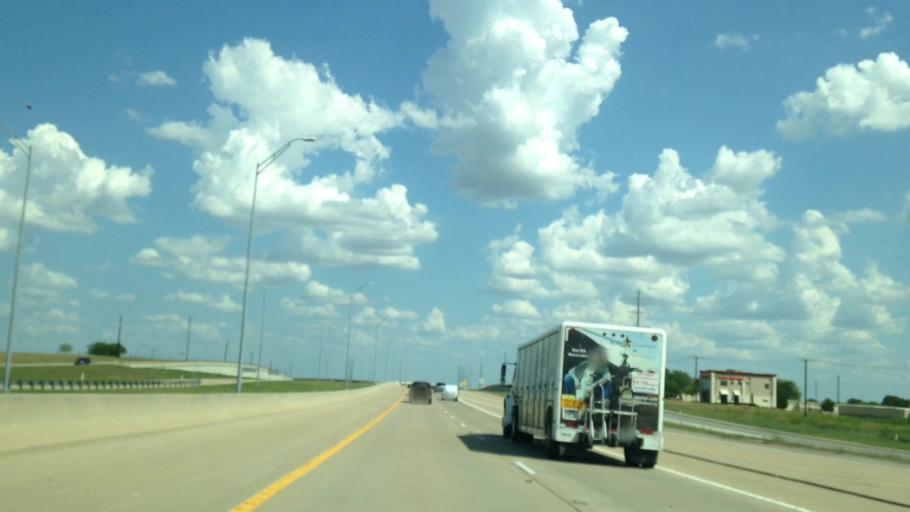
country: US
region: Texas
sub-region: Travis County
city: Pflugerville
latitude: 30.4801
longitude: -97.6060
